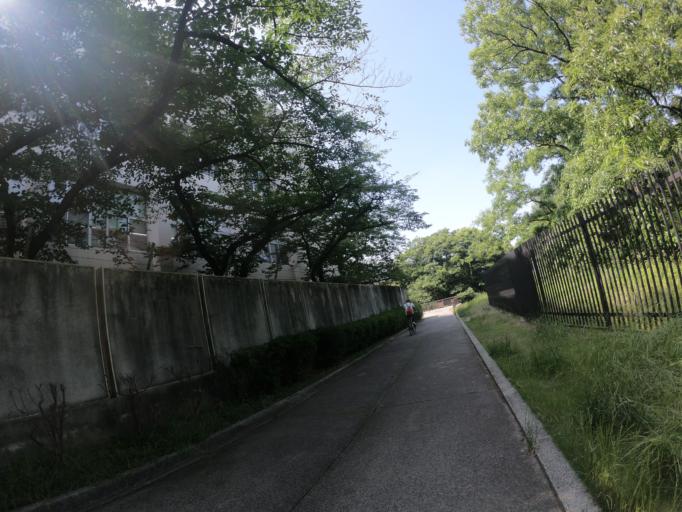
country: JP
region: Osaka
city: Sakai
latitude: 34.5653
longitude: 135.4839
